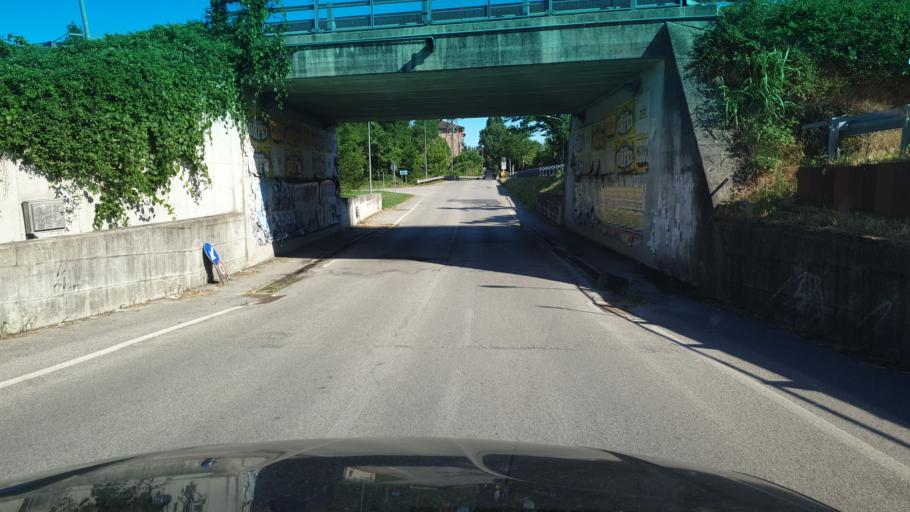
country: IT
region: Veneto
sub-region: Provincia di Rovigo
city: Rovigo
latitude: 45.0822
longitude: 11.7774
